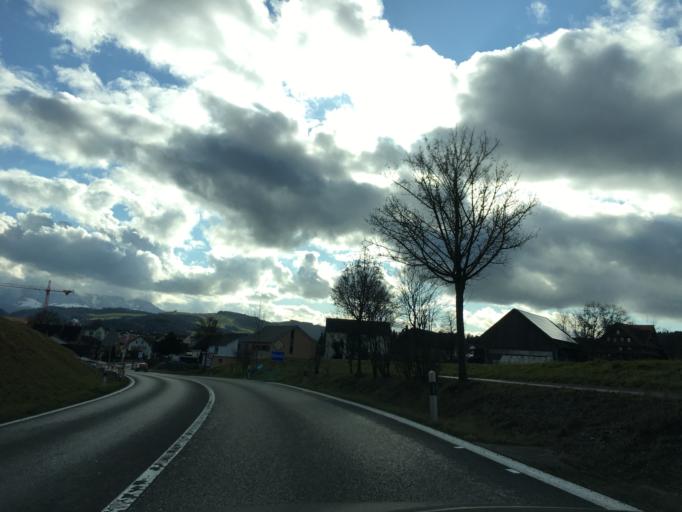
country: CH
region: Aargau
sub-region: Bezirk Muri
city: Oberruti
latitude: 47.1681
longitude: 8.3932
